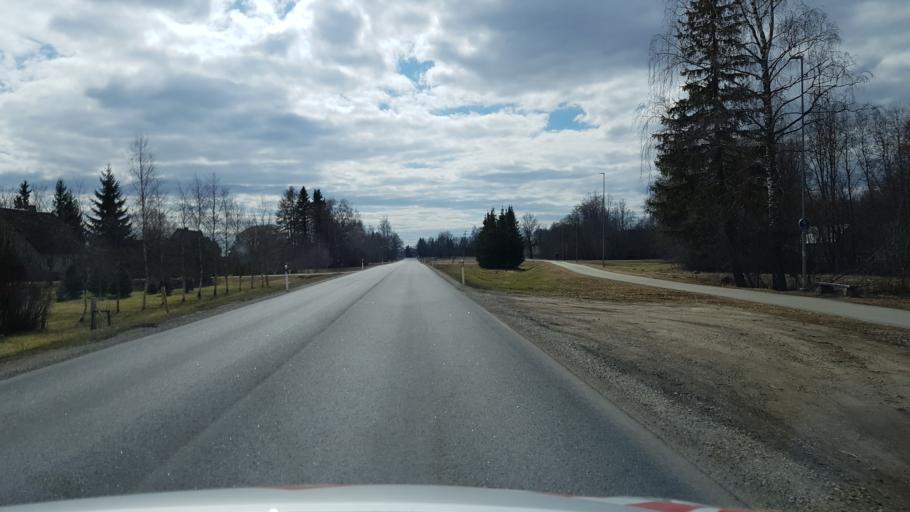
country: EE
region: Laeaene-Virumaa
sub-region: Vaeike-Maarja vald
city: Vaike-Maarja
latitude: 59.1228
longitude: 26.2481
